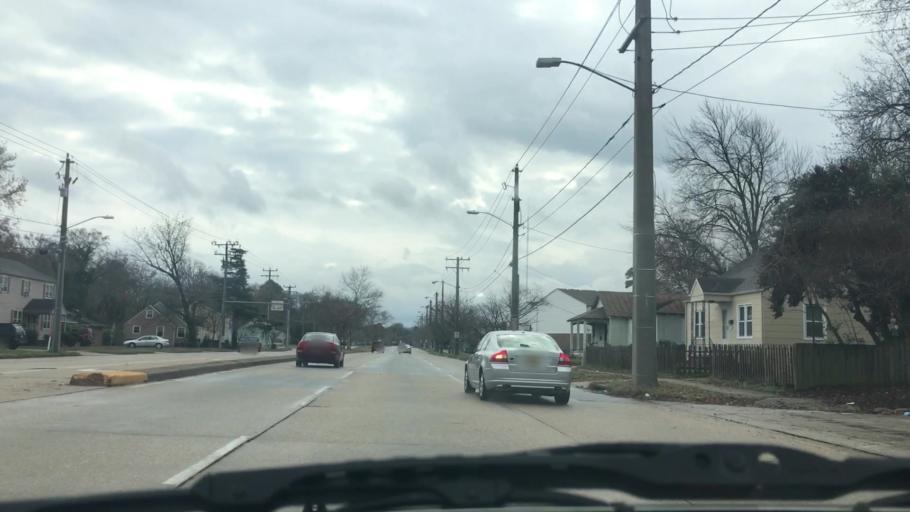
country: US
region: Virginia
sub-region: City of Norfolk
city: Norfolk
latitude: 36.8967
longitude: -76.2387
